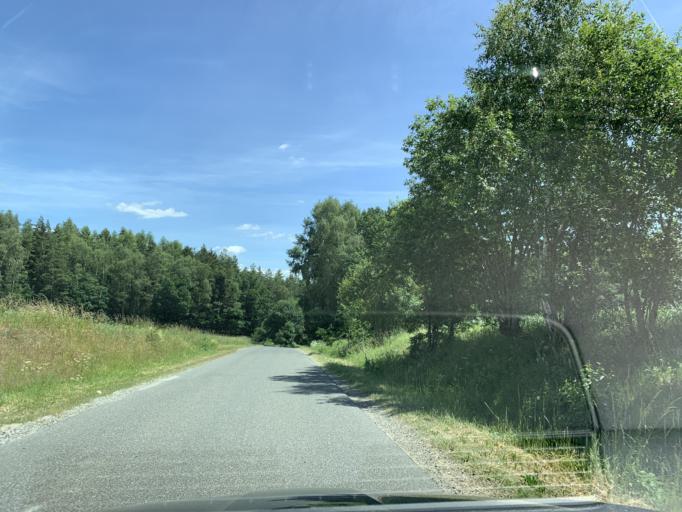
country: DE
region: Bavaria
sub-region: Upper Palatinate
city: Dieterskirchen
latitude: 49.4198
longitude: 12.4027
